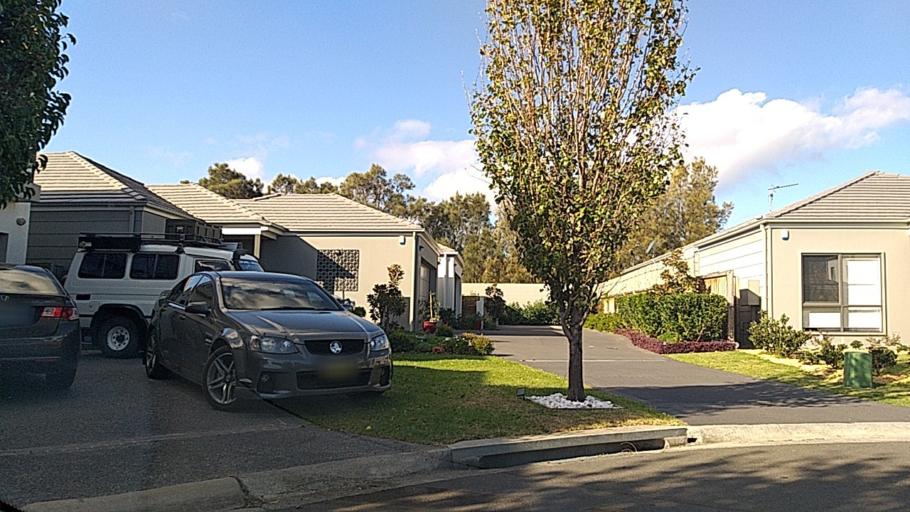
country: AU
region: New South Wales
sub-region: Wollongong
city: Corrimal
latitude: -34.3888
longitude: 150.9036
